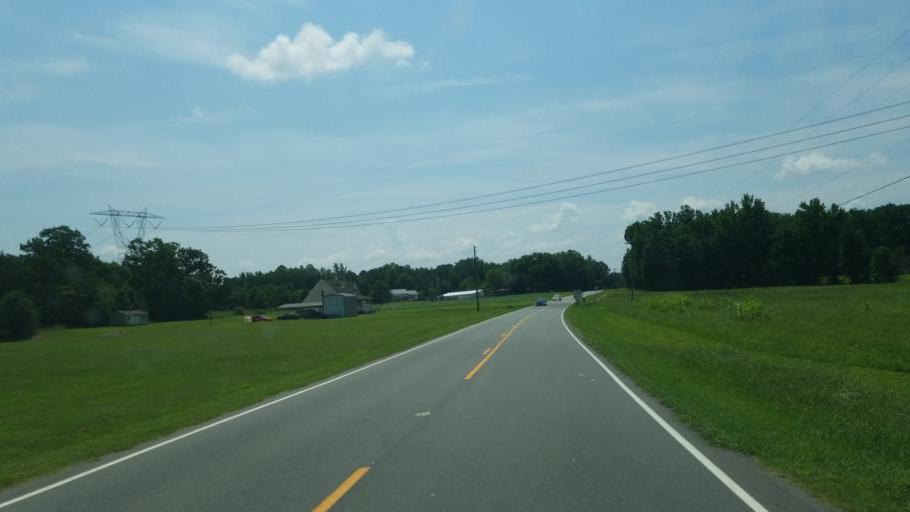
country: US
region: North Carolina
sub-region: Gaston County
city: Tryon
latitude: 35.3518
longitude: -81.3531
